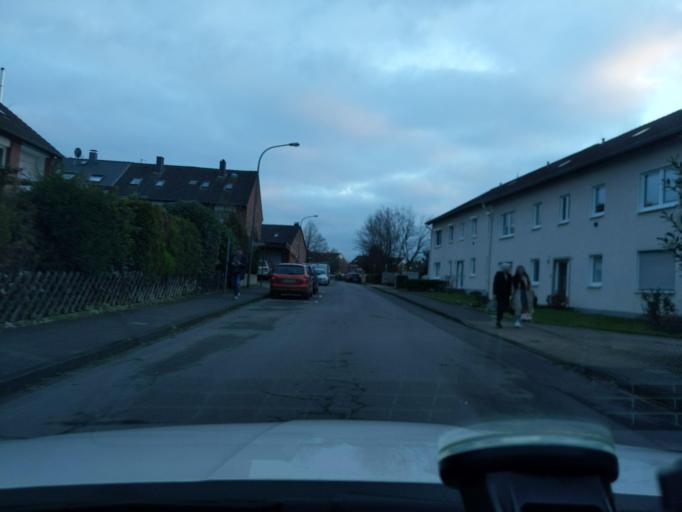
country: DE
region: North Rhine-Westphalia
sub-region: Regierungsbezirk Dusseldorf
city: Langenfeld
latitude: 51.1191
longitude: 6.9750
